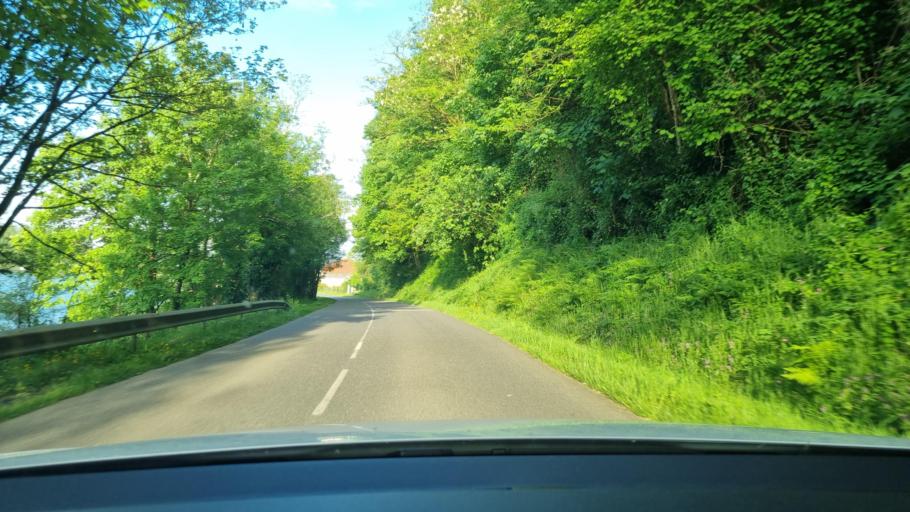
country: FR
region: Aquitaine
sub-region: Departement des Landes
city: Peyrehorade
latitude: 43.5357
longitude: -1.1509
